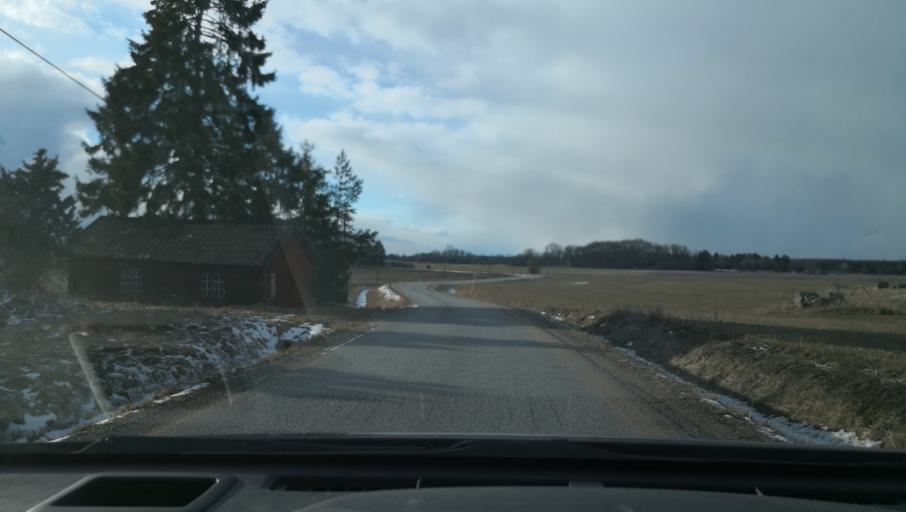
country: SE
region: Uppsala
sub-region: Enkopings Kommun
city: Irsta
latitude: 59.6966
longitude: 16.9550
